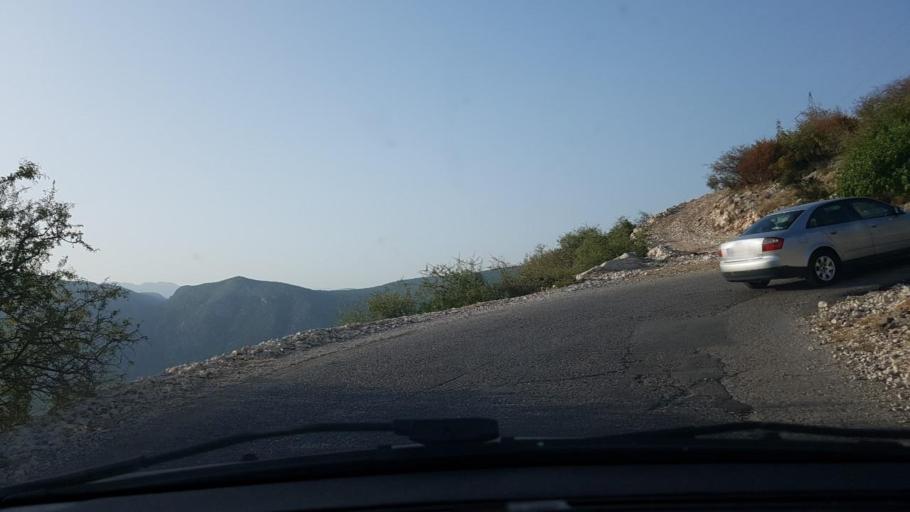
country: BA
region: Federation of Bosnia and Herzegovina
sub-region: Hercegovacko-Bosanski Kanton
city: Mostar
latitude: 43.3519
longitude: 17.8262
